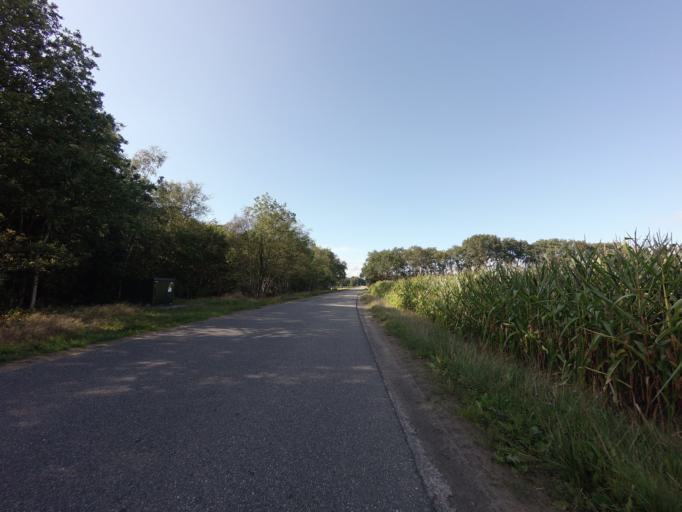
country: NL
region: Friesland
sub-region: Gemeente Heerenveen
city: Jubbega
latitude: 52.9776
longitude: 6.1849
